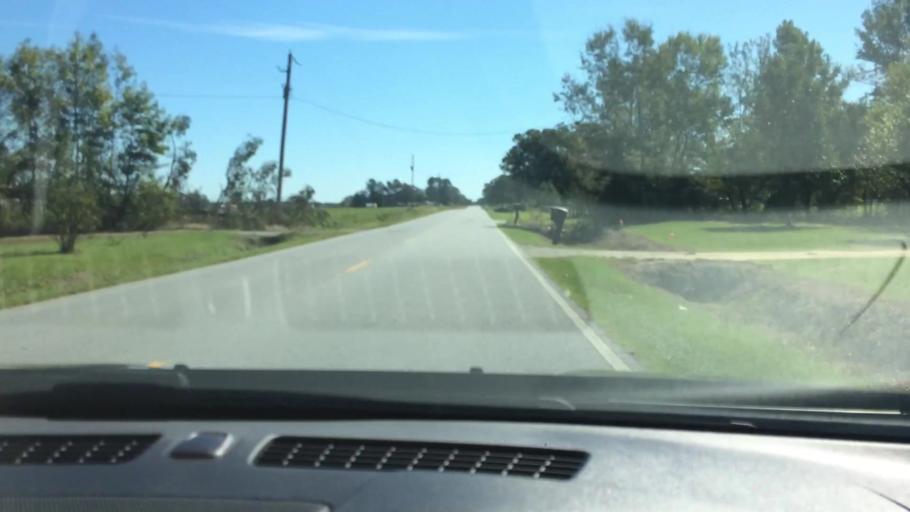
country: US
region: North Carolina
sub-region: Pitt County
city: Grifton
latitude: 35.3912
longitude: -77.3888
